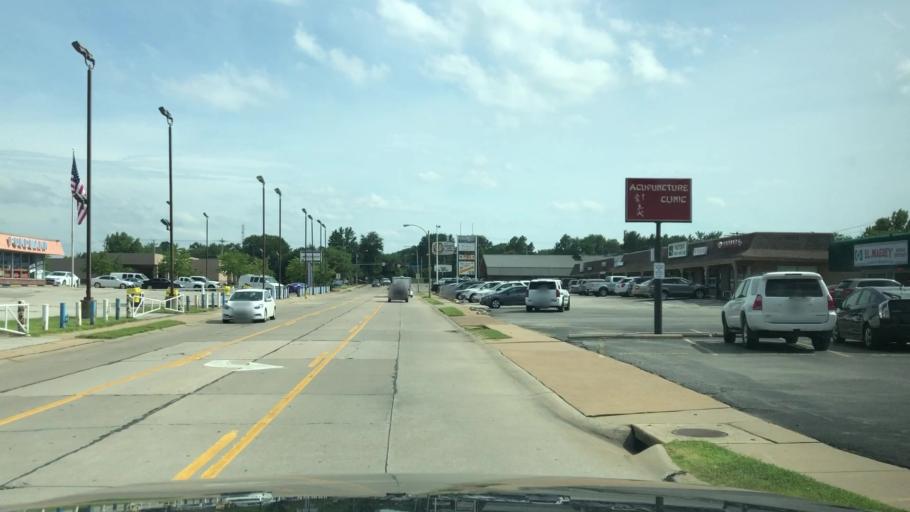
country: US
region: Missouri
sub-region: Saint Charles County
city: Saint Charles
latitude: 38.7865
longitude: -90.5156
